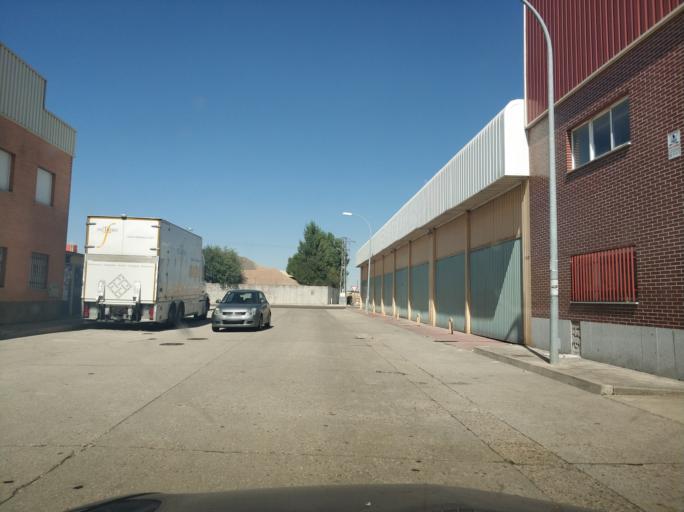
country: ES
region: Castille and Leon
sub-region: Provincia de Salamanca
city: Villares de la Reina
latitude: 40.9948
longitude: -5.6311
